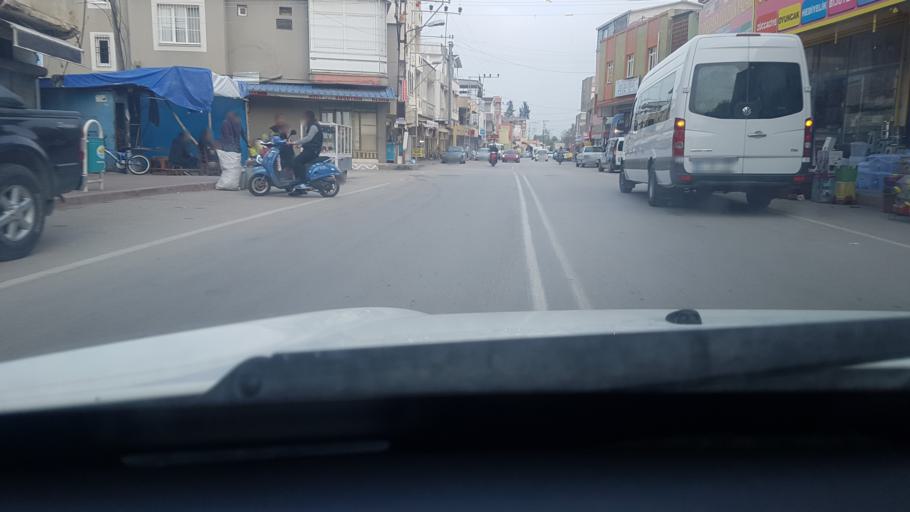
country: TR
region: Adana
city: Seyhan
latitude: 37.0144
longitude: 35.2773
